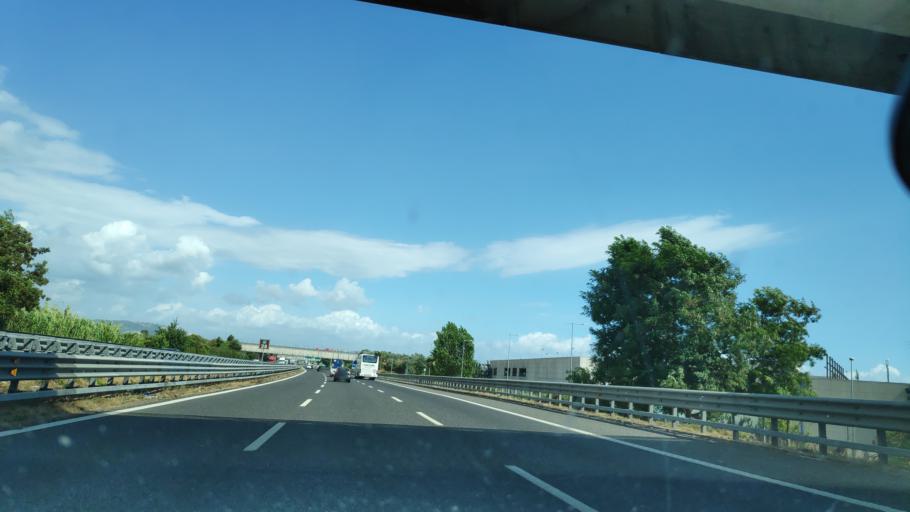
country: IT
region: Campania
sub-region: Provincia di Salerno
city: Sant'Antonio
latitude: 40.6374
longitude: 14.9072
